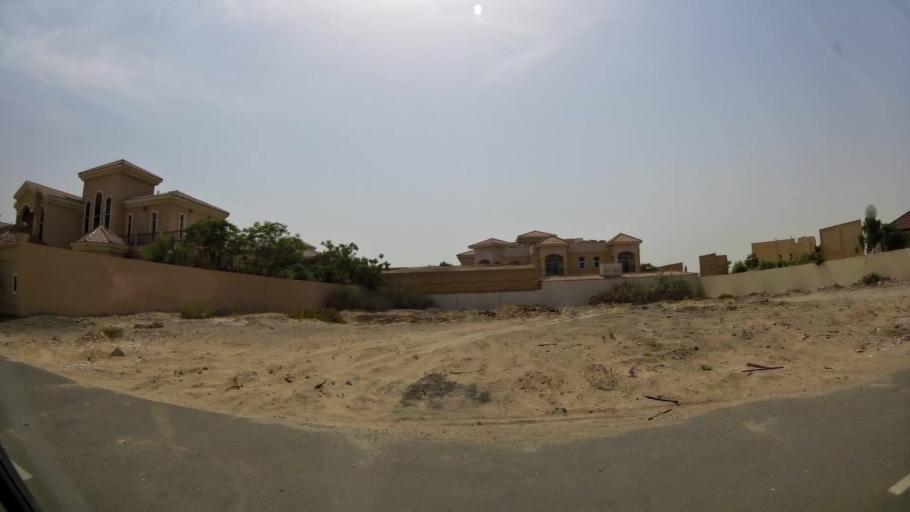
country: AE
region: Ash Shariqah
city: Sharjah
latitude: 25.2445
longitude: 55.4892
